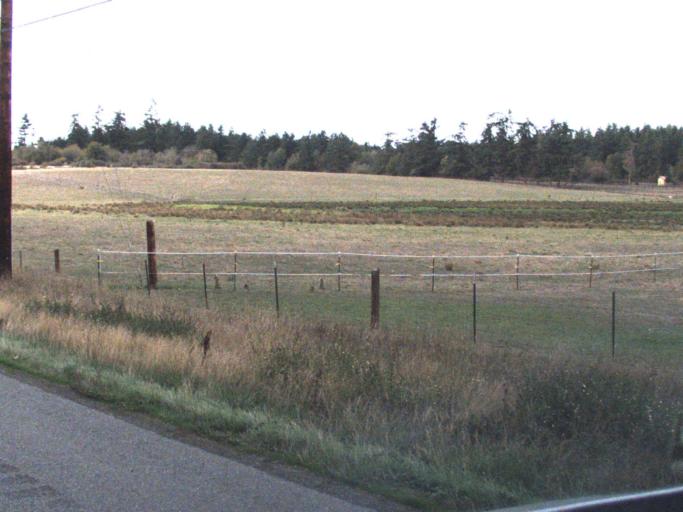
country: US
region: Washington
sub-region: Island County
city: Coupeville
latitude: 48.2628
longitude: -122.6880
